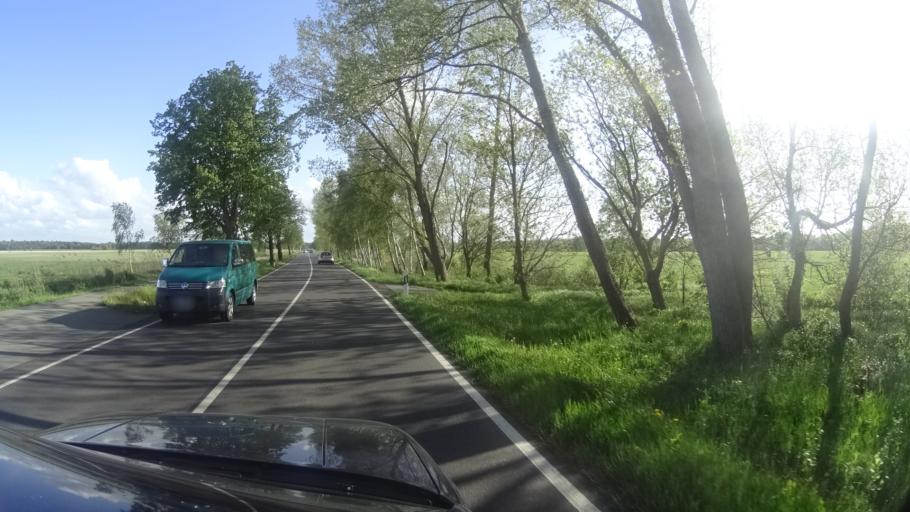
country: DE
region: Mecklenburg-Vorpommern
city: Ostseebad Dierhagen
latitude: 54.2697
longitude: 12.3565
